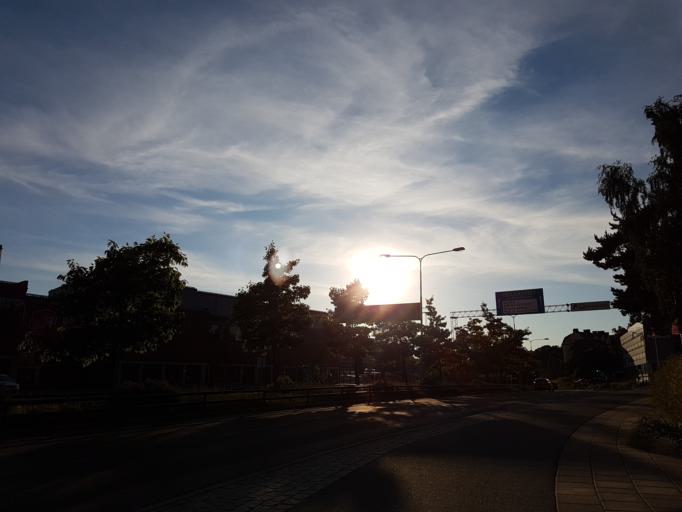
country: SE
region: Stockholm
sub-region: Solna Kommun
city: Solna
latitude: 59.3541
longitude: 18.0169
